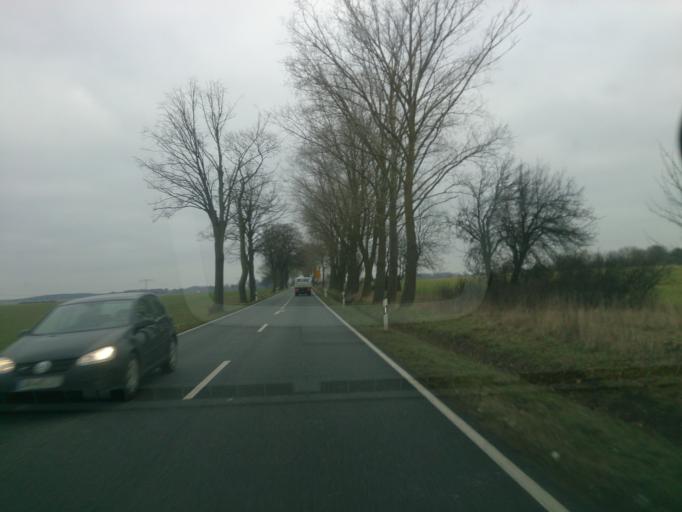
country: DE
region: Mecklenburg-Vorpommern
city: Borrentin
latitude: 53.8293
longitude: 12.9860
